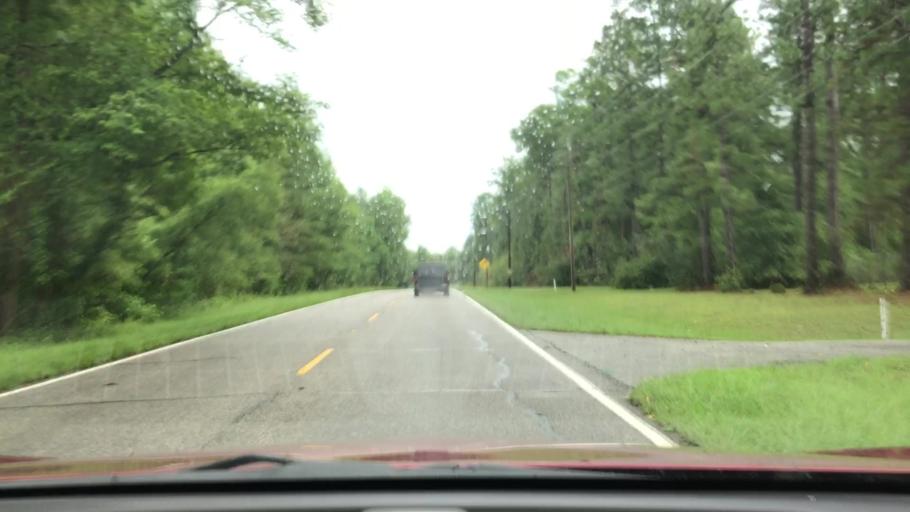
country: US
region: South Carolina
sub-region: Georgetown County
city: Georgetown
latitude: 33.4546
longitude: -79.2804
